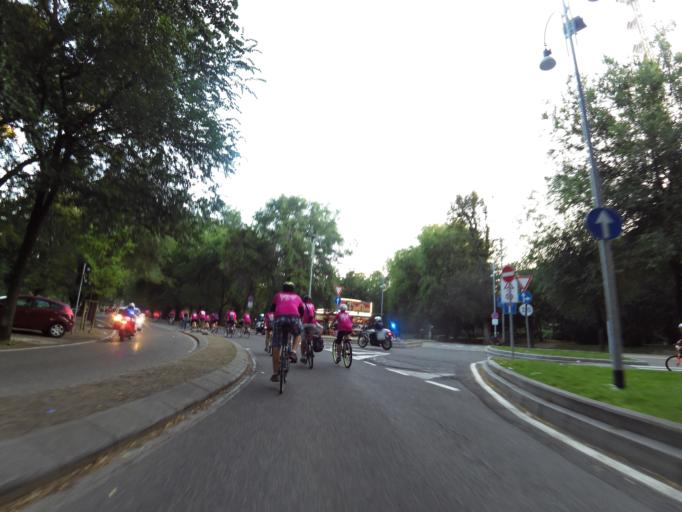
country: IT
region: Lombardy
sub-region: Citta metropolitana di Milano
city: Milano
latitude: 45.4725
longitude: 9.1722
